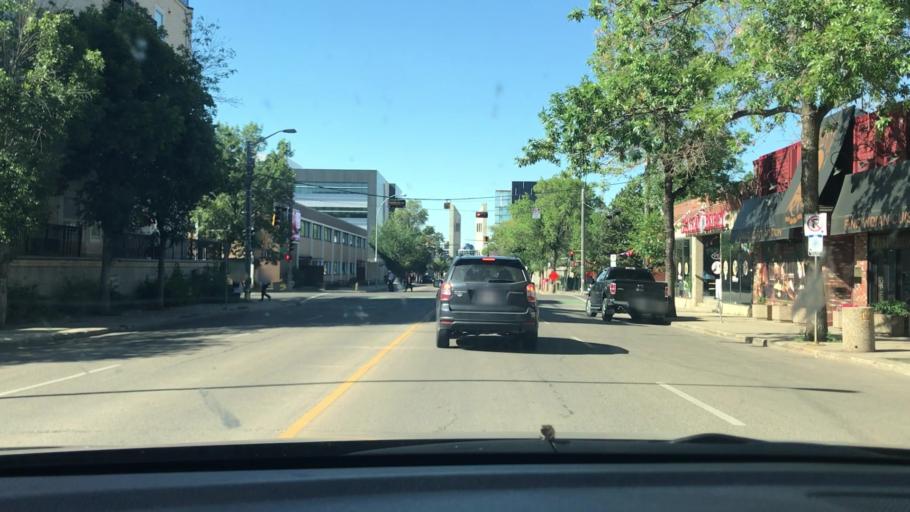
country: CA
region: Alberta
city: Edmonton
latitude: 53.5425
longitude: -113.5048
